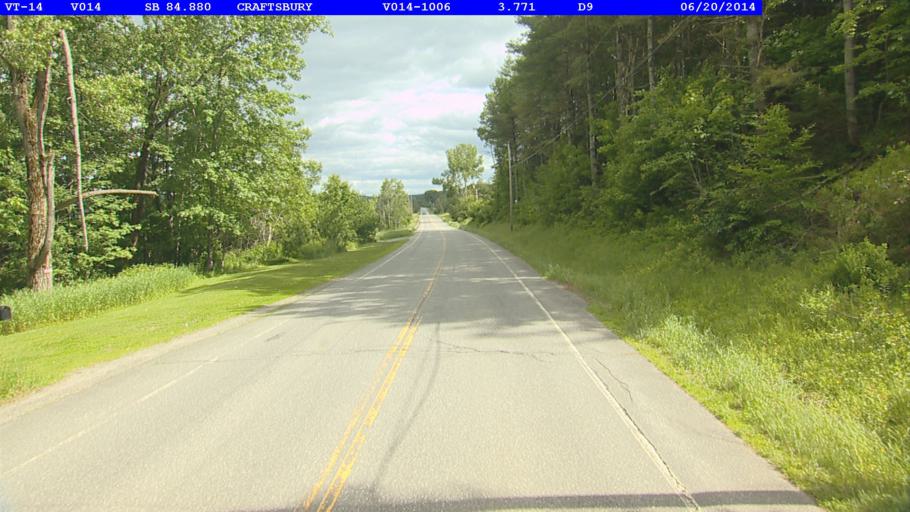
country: US
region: Vermont
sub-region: Caledonia County
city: Hardwick
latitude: 44.6453
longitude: -72.4032
